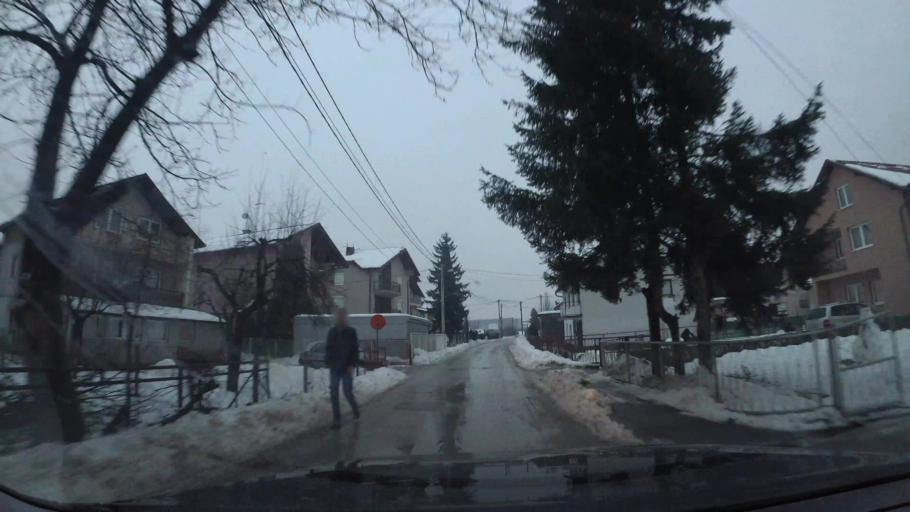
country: BA
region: Federation of Bosnia and Herzegovina
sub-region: Kanton Sarajevo
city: Sarajevo
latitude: 43.8384
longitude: 18.3019
